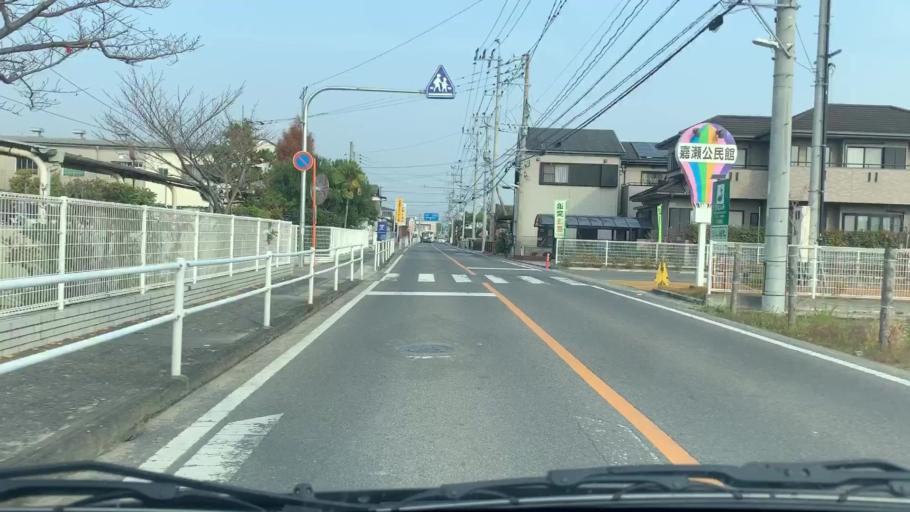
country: JP
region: Saga Prefecture
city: Saga-shi
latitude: 33.2410
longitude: 130.2583
